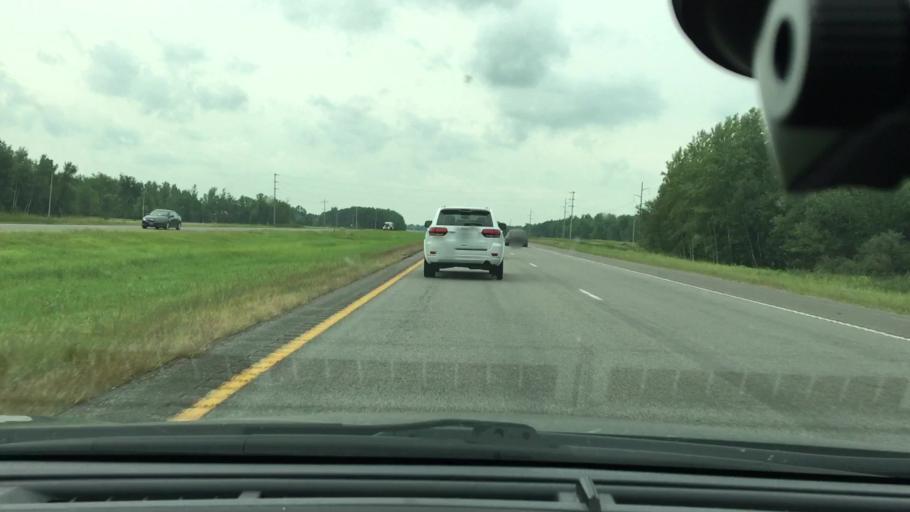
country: US
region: Minnesota
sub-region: Mille Lacs County
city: Milaca
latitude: 45.7452
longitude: -93.6358
